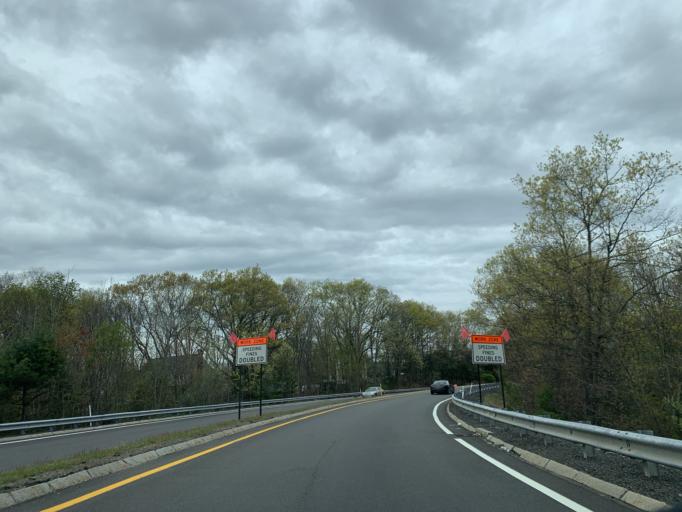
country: US
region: Massachusetts
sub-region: Bristol County
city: Attleboro
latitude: 41.9352
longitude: -71.3210
